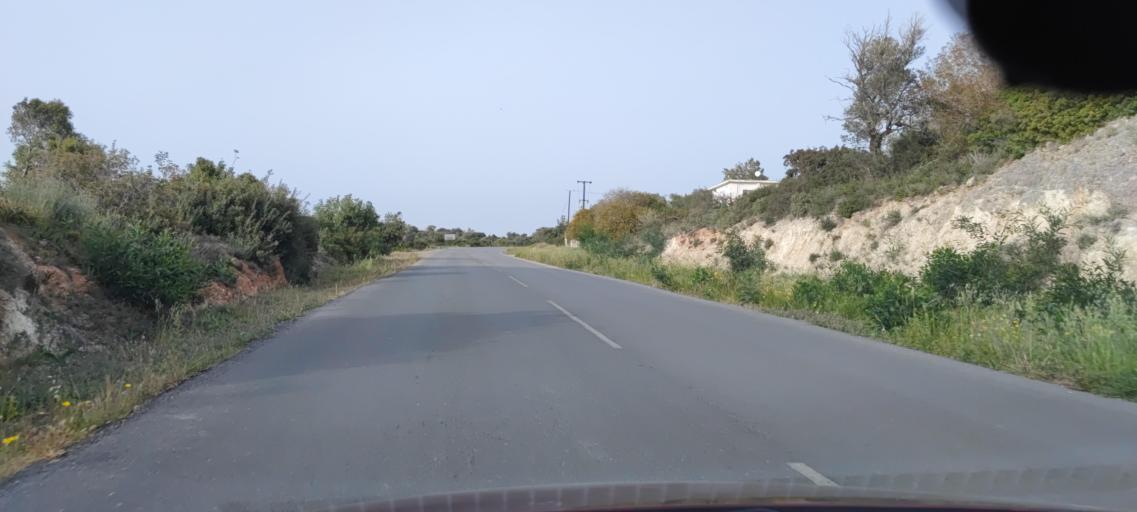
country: CY
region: Ammochostos
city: Leonarisso
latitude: 35.5188
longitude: 34.1699
